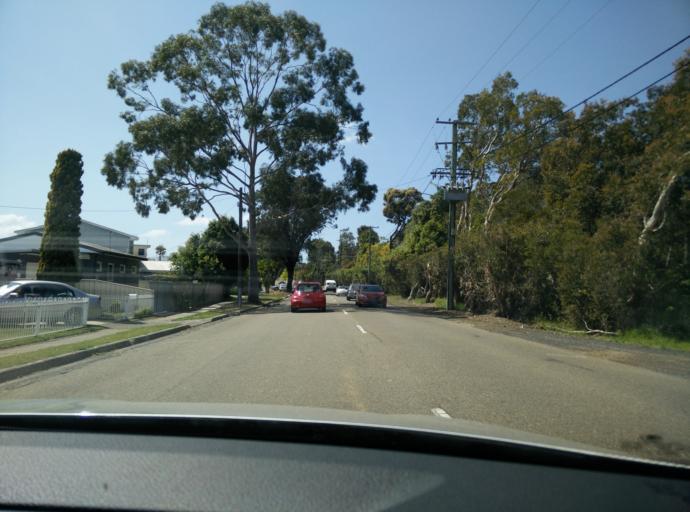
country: AU
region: New South Wales
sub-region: Gosford Shire
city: Blackwall
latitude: -33.4970
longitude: 151.3048
